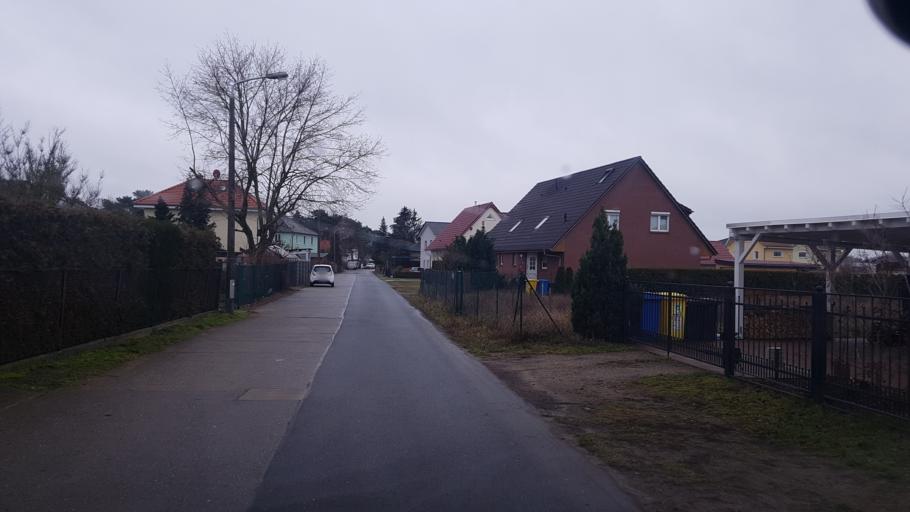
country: DE
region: Berlin
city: Wannsee
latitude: 52.3595
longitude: 13.1285
